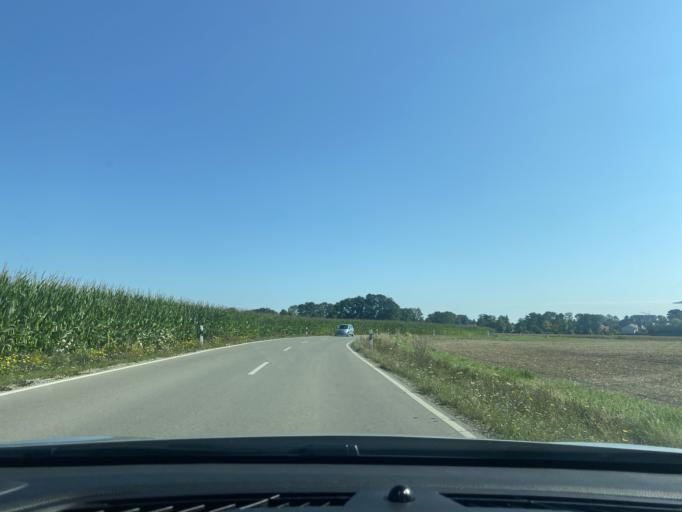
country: DE
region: Bavaria
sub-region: Upper Bavaria
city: Worth
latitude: 48.2733
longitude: 11.9040
